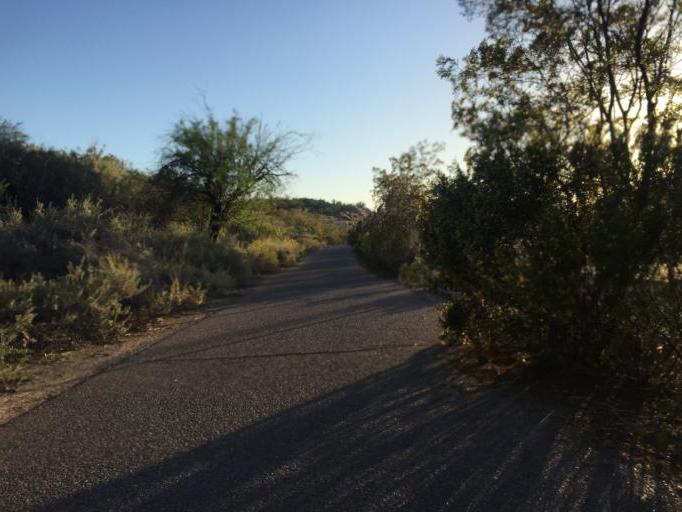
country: US
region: Arizona
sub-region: Maricopa County
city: Paradise Valley
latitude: 33.5750
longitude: -112.0141
